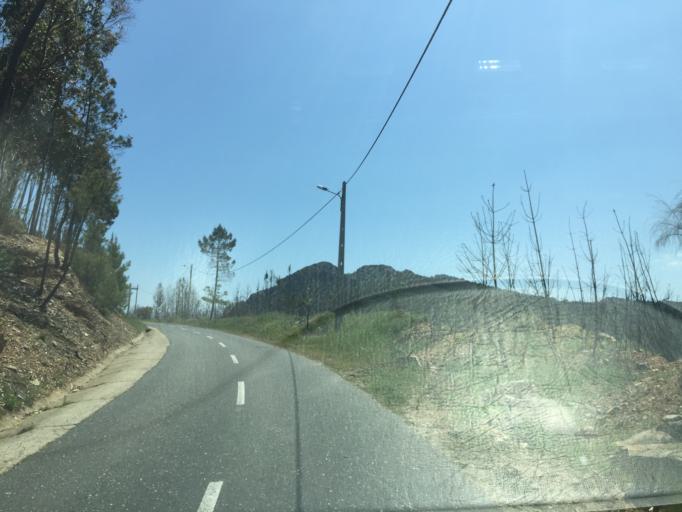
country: PT
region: Coimbra
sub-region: Pampilhosa da Serra
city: Pampilhosa da Serra
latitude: 40.0876
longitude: -7.8743
